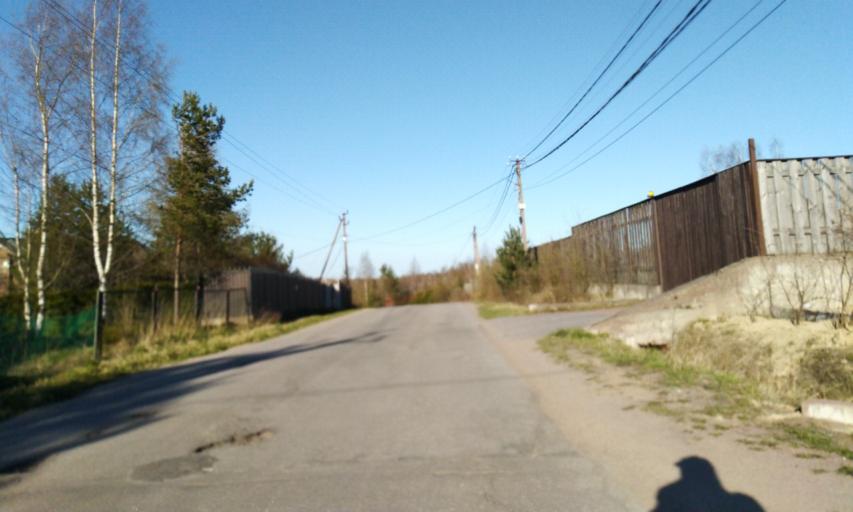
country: RU
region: Leningrad
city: Toksovo
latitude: 60.1463
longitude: 30.5672
